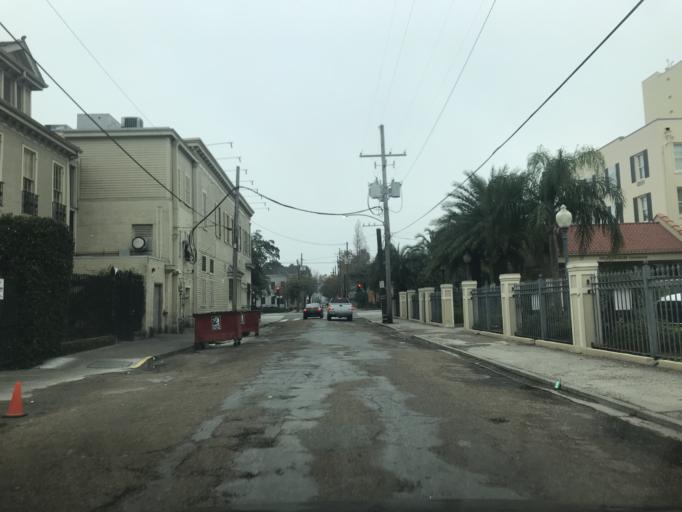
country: US
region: Louisiana
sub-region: Orleans Parish
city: New Orleans
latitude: 29.9402
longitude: -90.0738
